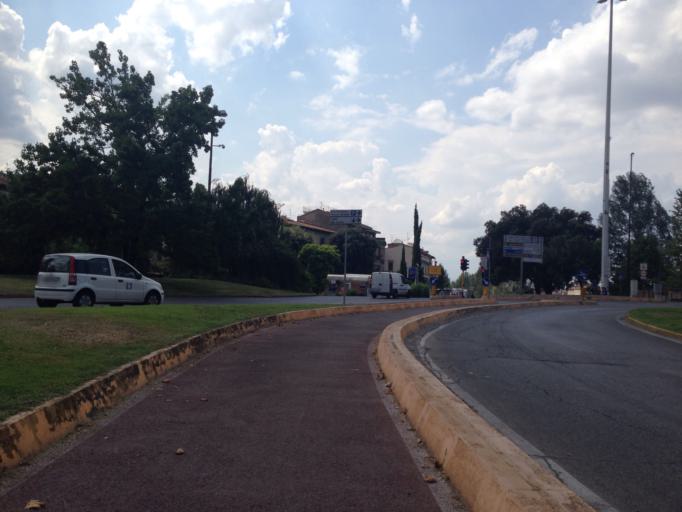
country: IT
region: Tuscany
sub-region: Province of Florence
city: Florence
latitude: 43.7640
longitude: 11.2715
